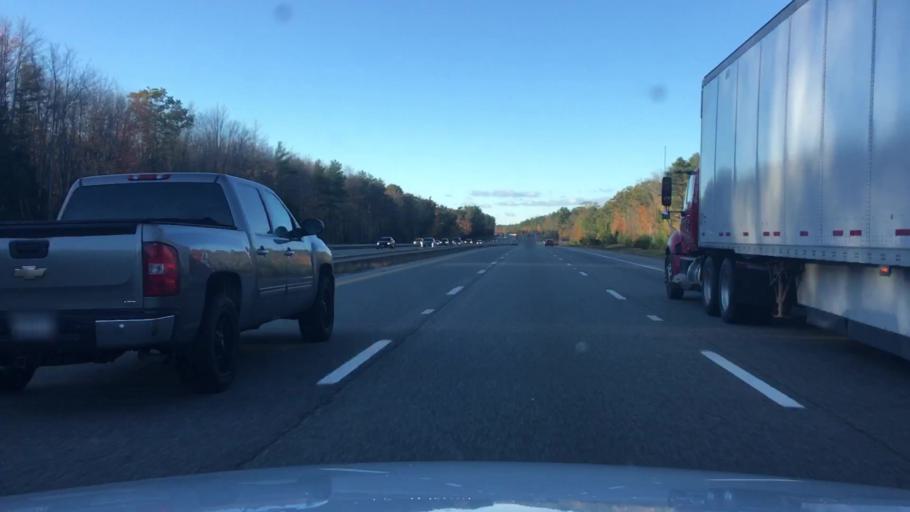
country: US
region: Maine
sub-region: York County
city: West Kennebunk
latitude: 43.4343
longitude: -70.5445
